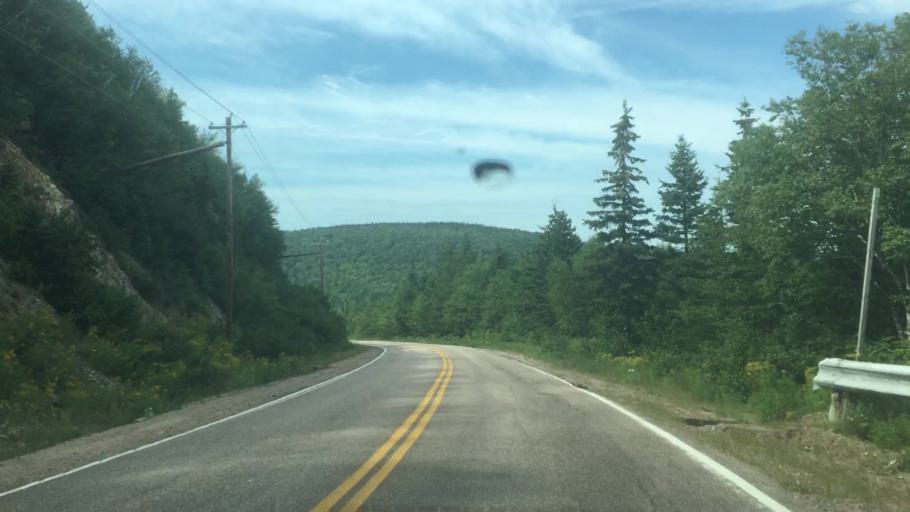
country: CA
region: Nova Scotia
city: Sydney Mines
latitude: 46.6036
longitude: -60.3863
